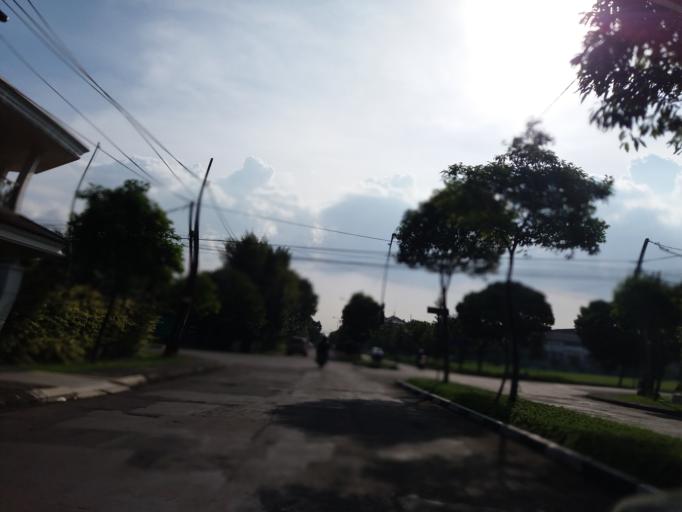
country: ID
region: West Java
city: Bandung
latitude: -6.9592
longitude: 107.6281
